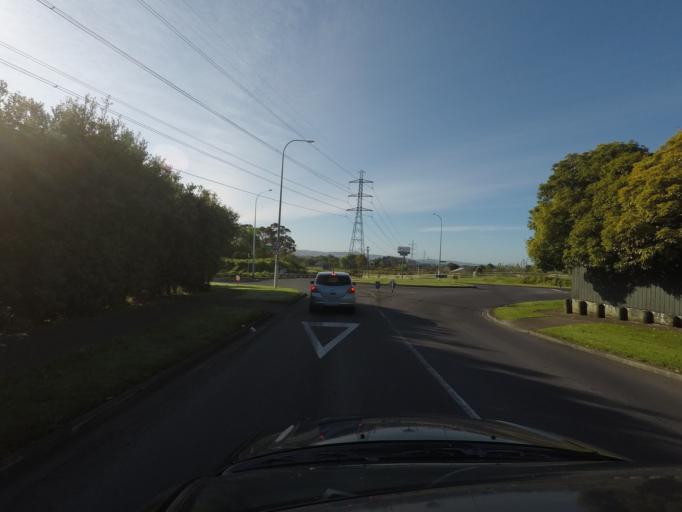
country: NZ
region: Auckland
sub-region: Auckland
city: Takanini
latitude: -37.0154
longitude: 174.9208
